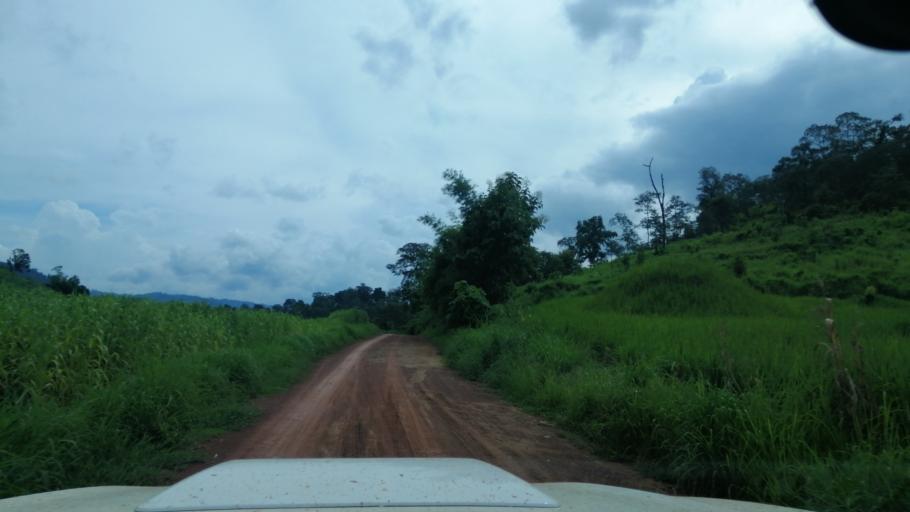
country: TH
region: Nan
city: Mae Charim
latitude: 18.7760
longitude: 101.3170
